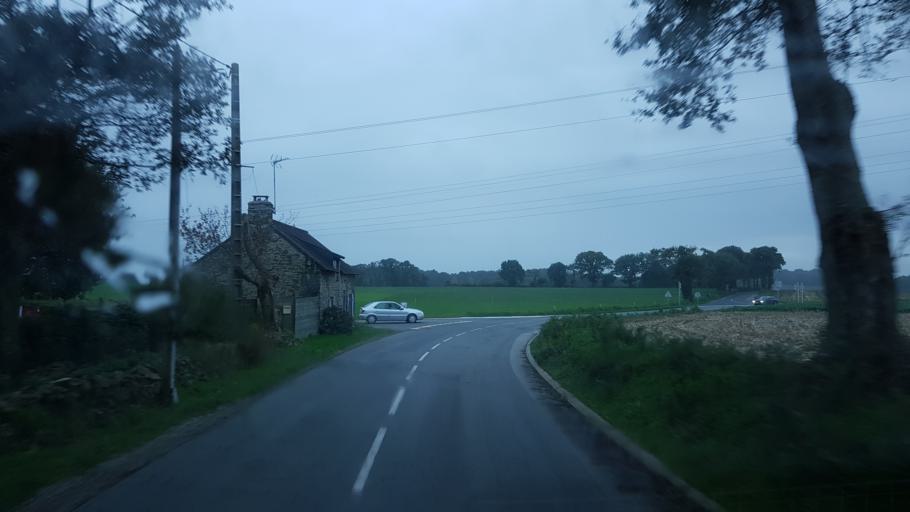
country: FR
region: Brittany
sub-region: Departement du Morbihan
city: Trefflean
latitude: 47.6581
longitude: -2.6258
